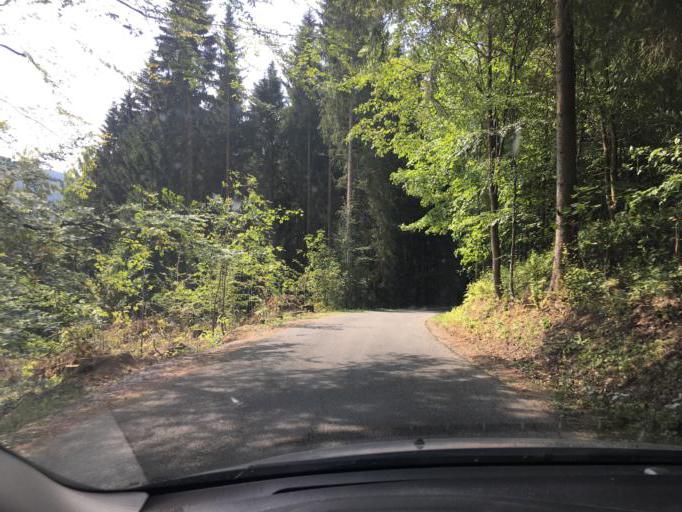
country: CZ
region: Kralovehradecky
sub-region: Okres Trutnov
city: Spindleruv Mlyn
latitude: 50.7281
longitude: 15.5916
